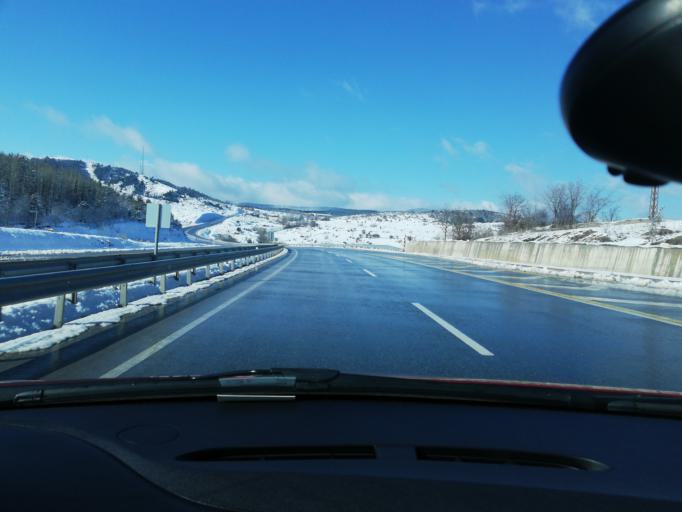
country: TR
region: Kastamonu
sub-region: Cide
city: Kastamonu
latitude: 41.3605
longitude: 33.6814
